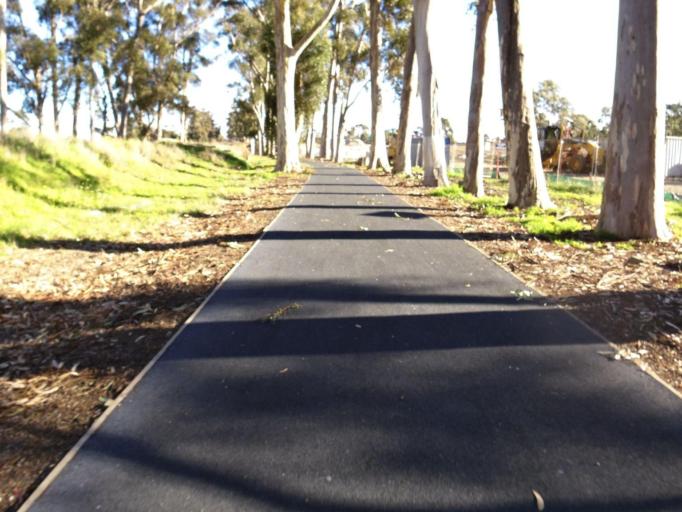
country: AU
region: Victoria
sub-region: Whittlesea
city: Mill Park
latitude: -37.6443
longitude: 145.0851
